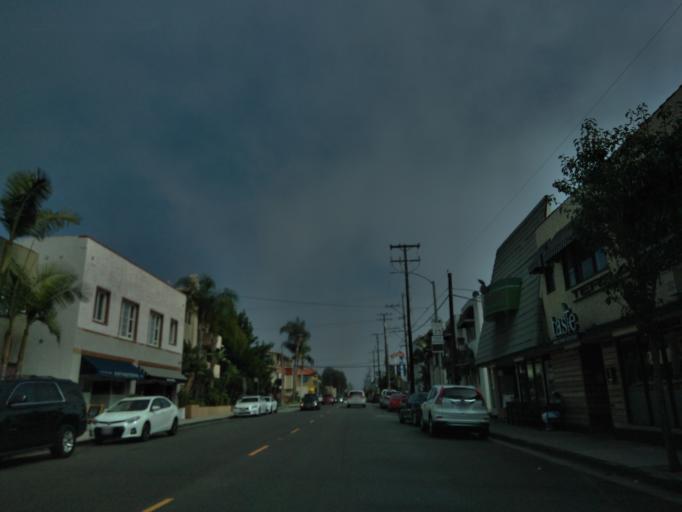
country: US
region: California
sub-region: Los Angeles County
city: Long Beach
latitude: 33.7644
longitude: -118.1511
